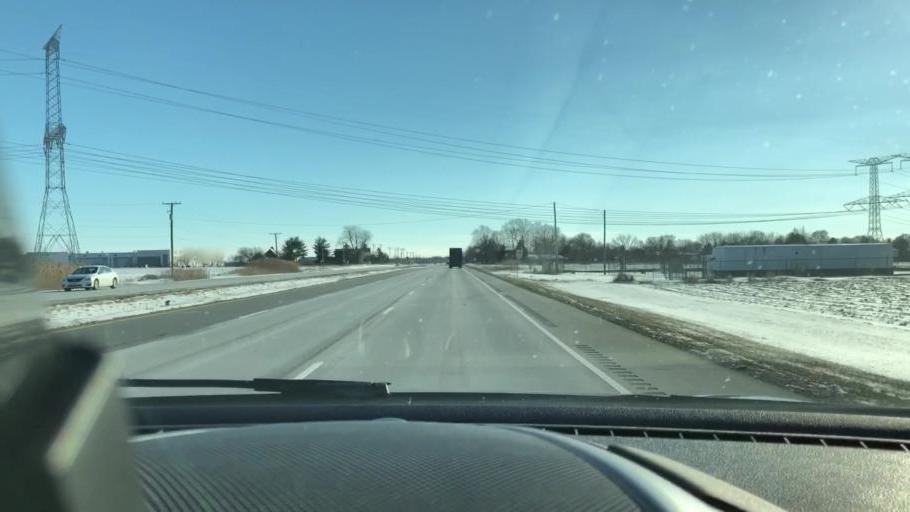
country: US
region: Illinois
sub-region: Will County
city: Preston Heights
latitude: 41.4568
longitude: -88.0794
